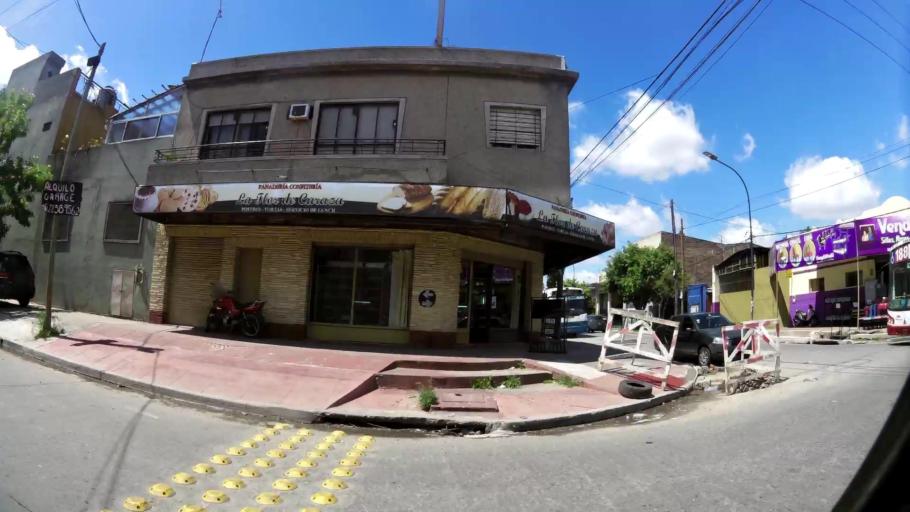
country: AR
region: Buenos Aires
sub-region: Partido de Lanus
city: Lanus
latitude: -34.7011
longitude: -58.4257
